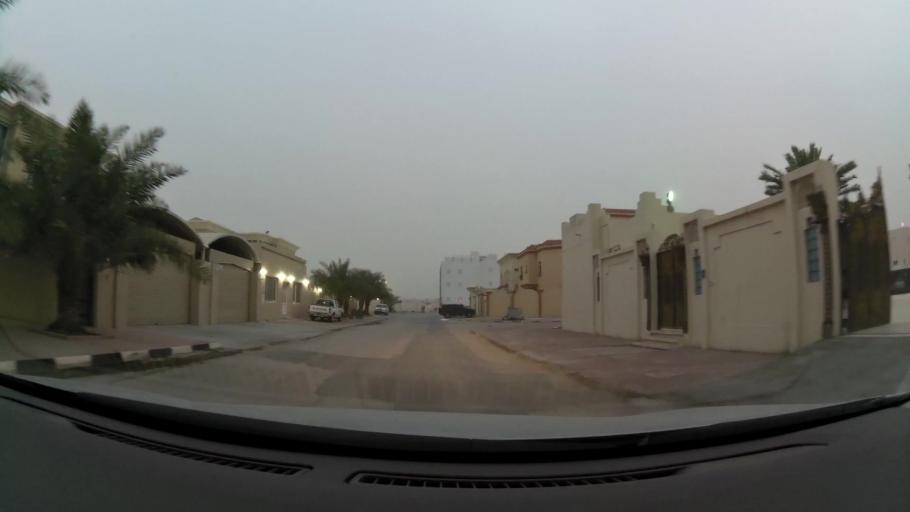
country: QA
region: Baladiyat ad Dawhah
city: Doha
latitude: 25.2289
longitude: 51.4934
